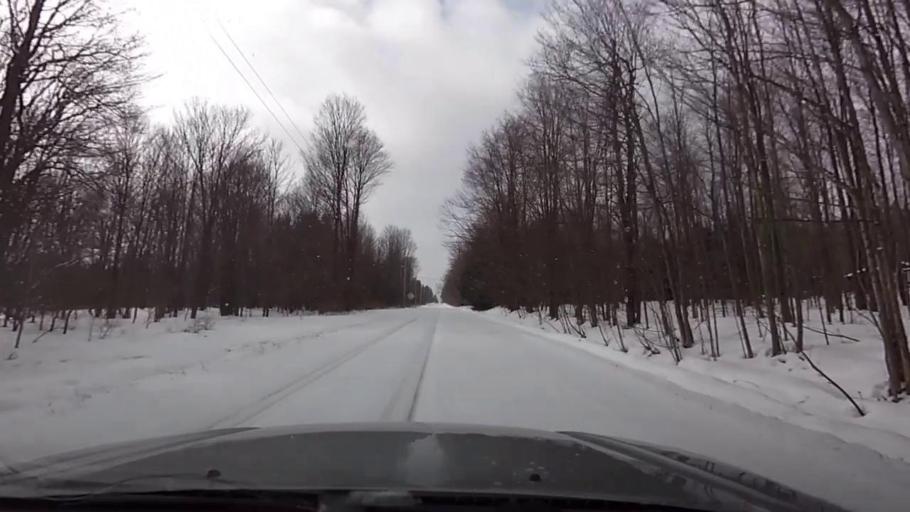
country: US
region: New York
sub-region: Cattaraugus County
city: Franklinville
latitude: 42.3362
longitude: -78.3540
